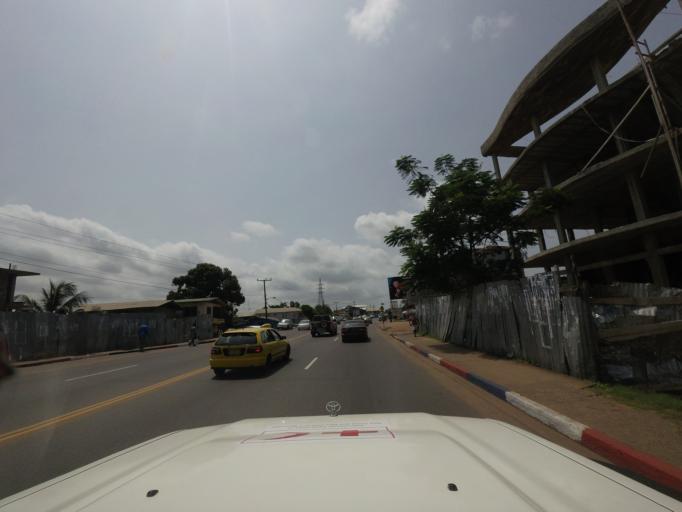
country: LR
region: Montserrado
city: Monrovia
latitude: 6.2887
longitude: -10.7716
